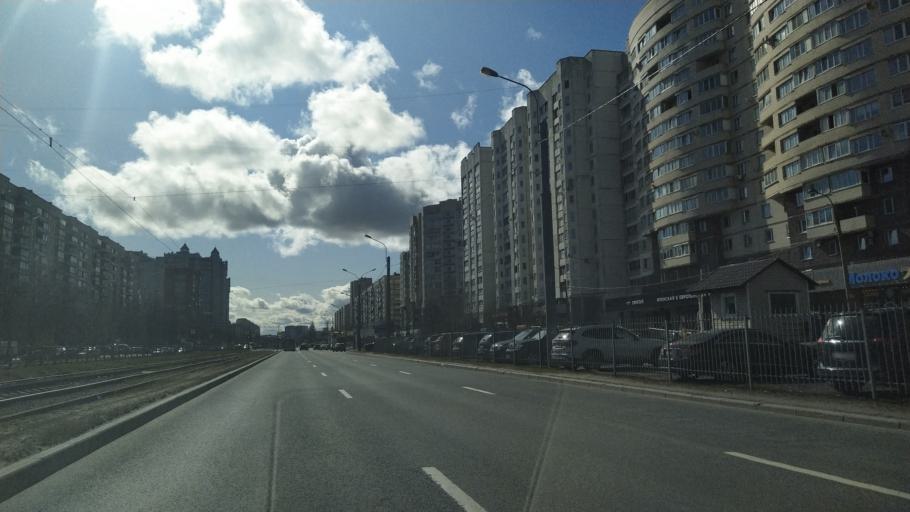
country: RU
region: St.-Petersburg
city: Ozerki
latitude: 60.0489
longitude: 30.3318
